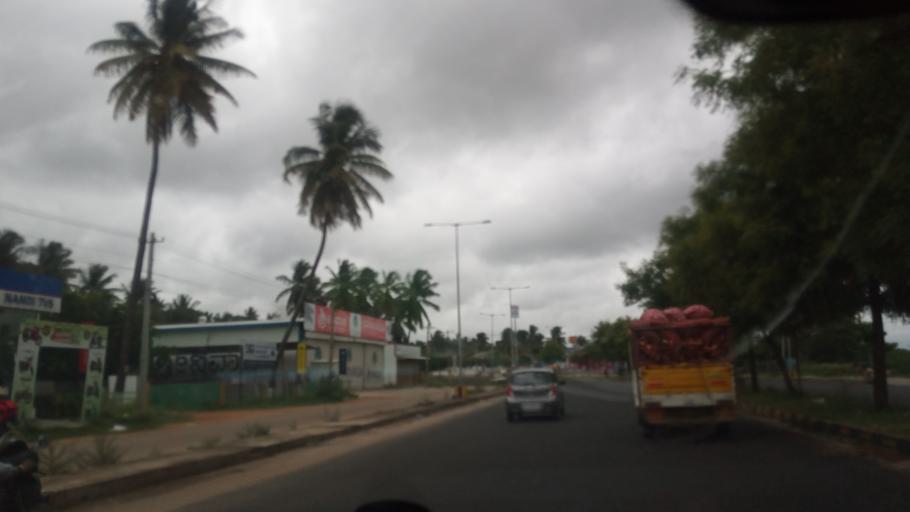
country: IN
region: Karnataka
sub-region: Mysore
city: Mysore
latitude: 12.3056
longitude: 76.6019
